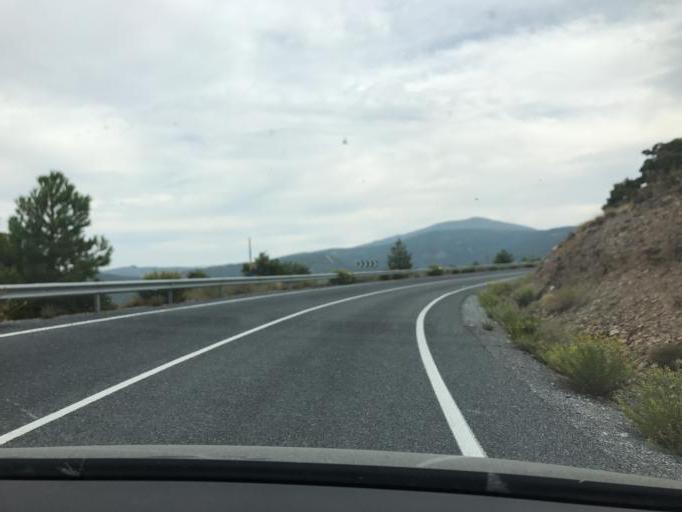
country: ES
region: Andalusia
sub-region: Provincia de Granada
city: Ferreira
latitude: 37.1471
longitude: -3.0458
